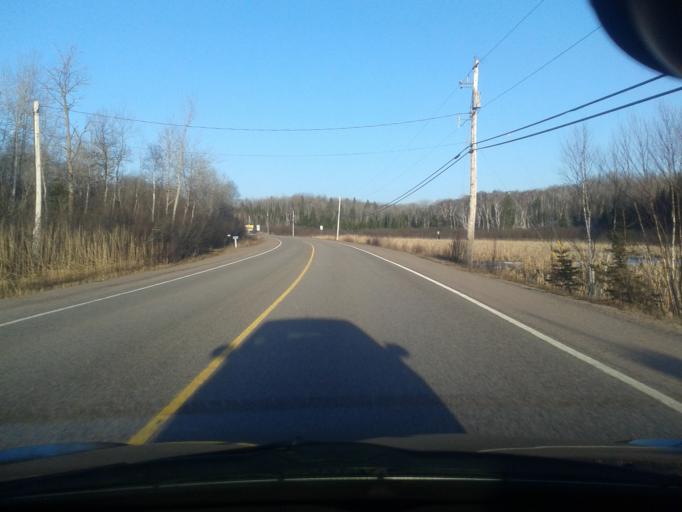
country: CA
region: Ontario
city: Powassan
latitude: 46.1892
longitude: -79.3039
